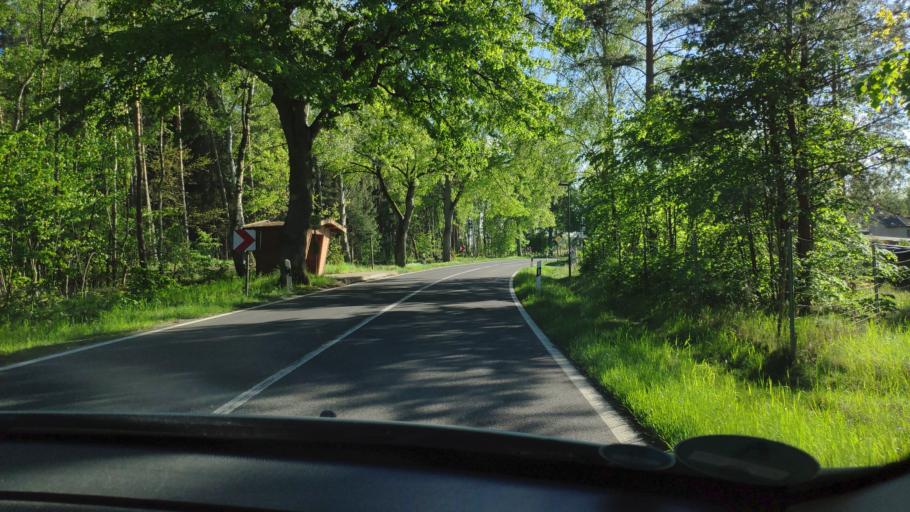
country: DE
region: Mecklenburg-Vorpommern
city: Rechlin
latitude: 53.3013
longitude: 12.8175
